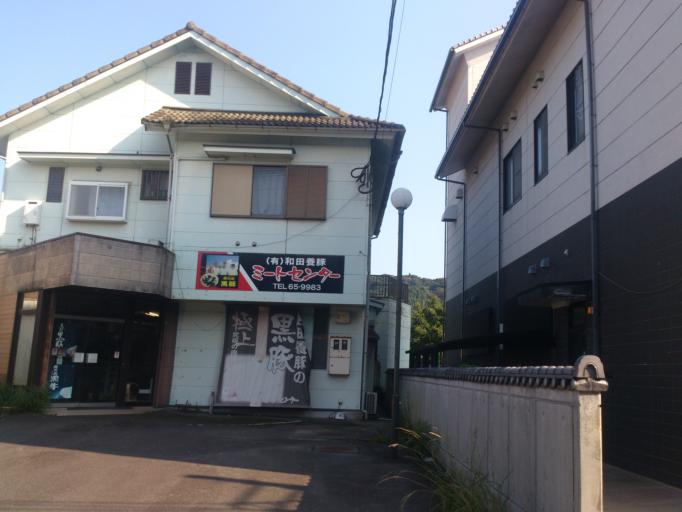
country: JP
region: Kagoshima
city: Kanoya
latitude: 31.3473
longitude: 130.9464
